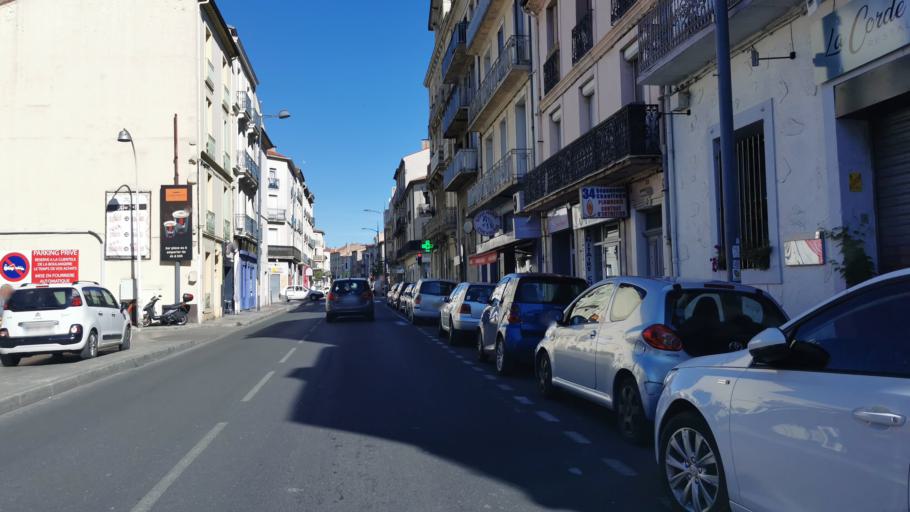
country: FR
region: Languedoc-Roussillon
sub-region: Departement de l'Herault
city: Beziers
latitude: 43.3476
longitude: 3.2176
